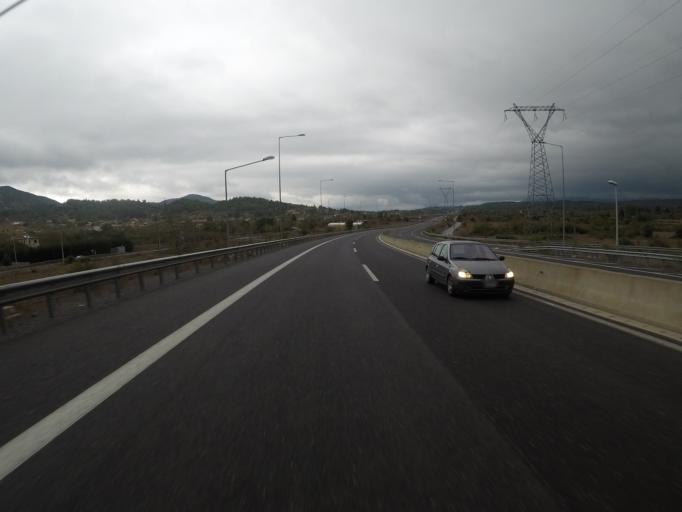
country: GR
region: Peloponnese
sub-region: Nomos Arkadias
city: Tripoli
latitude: 37.4631
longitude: 22.3278
